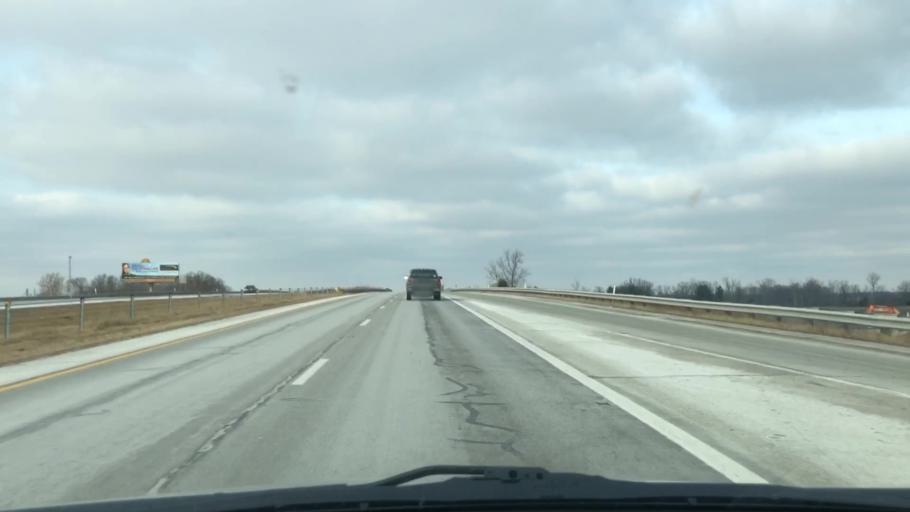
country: US
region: Indiana
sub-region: DeKalb County
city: Waterloo
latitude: 41.5288
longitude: -85.0555
